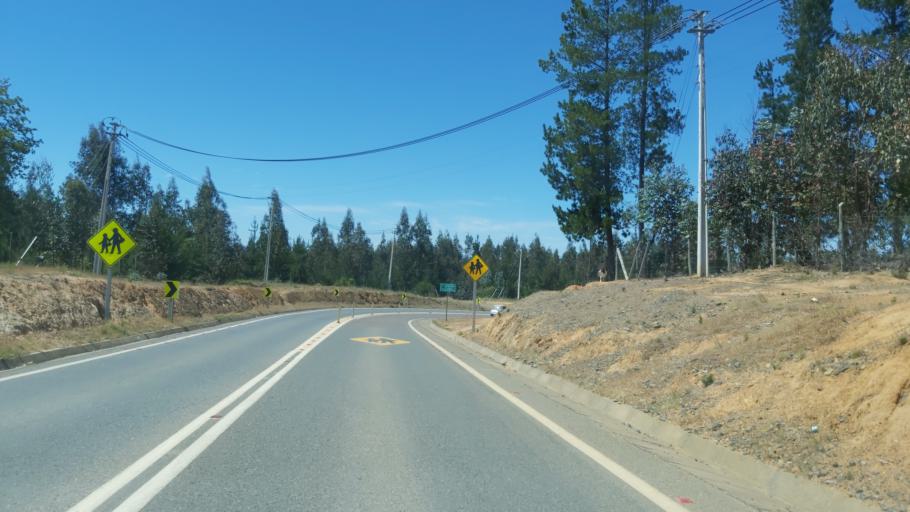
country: CL
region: Maule
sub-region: Provincia de Talca
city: Talca
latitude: -34.9625
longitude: -71.9607
